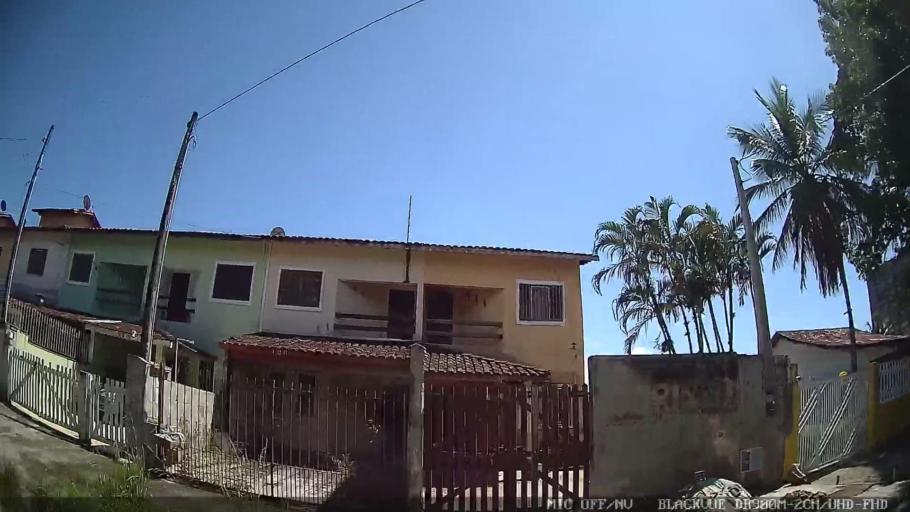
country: BR
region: Sao Paulo
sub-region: Caraguatatuba
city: Caraguatatuba
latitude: -23.6820
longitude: -45.4338
